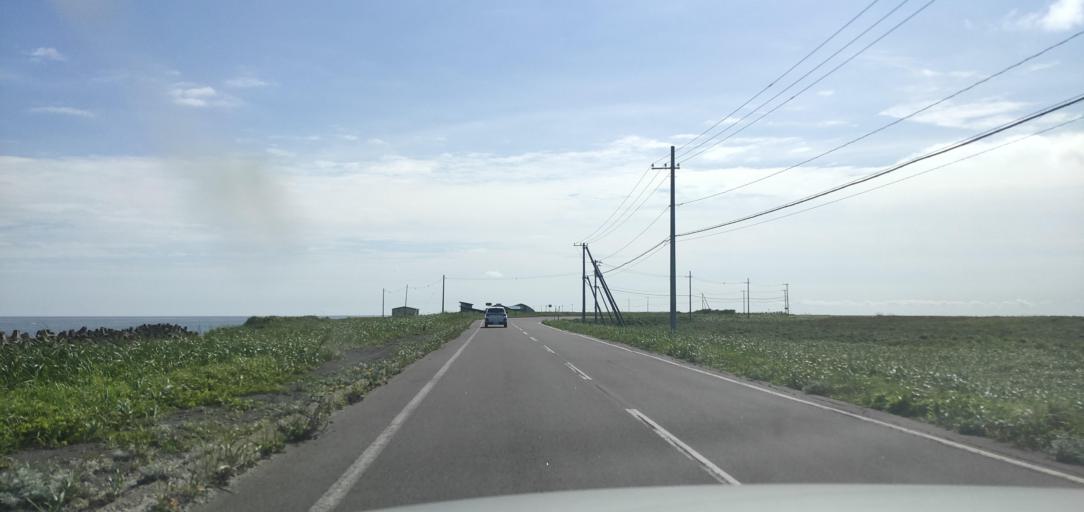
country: JP
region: Hokkaido
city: Shibetsu
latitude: 43.6265
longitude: 145.2036
